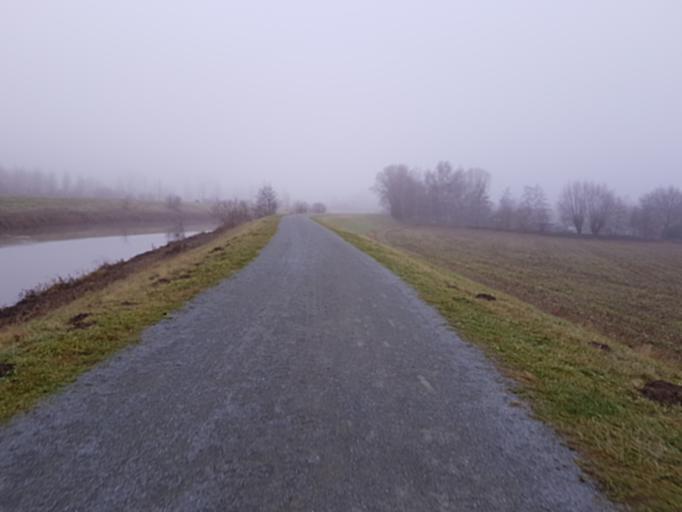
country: BE
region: Flanders
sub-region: Provincie Antwerpen
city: Bonheiden
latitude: 51.0058
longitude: 4.5347
